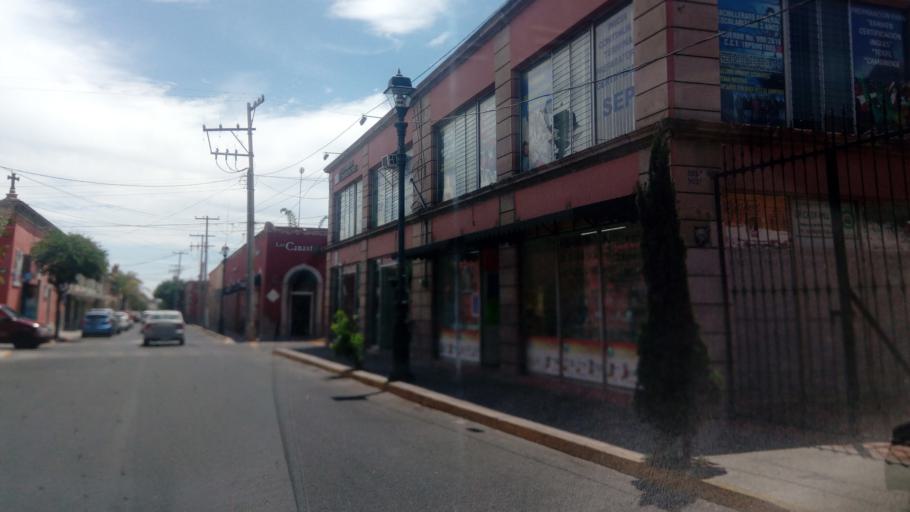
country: MX
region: Durango
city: Victoria de Durango
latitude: 24.0258
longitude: -104.6697
